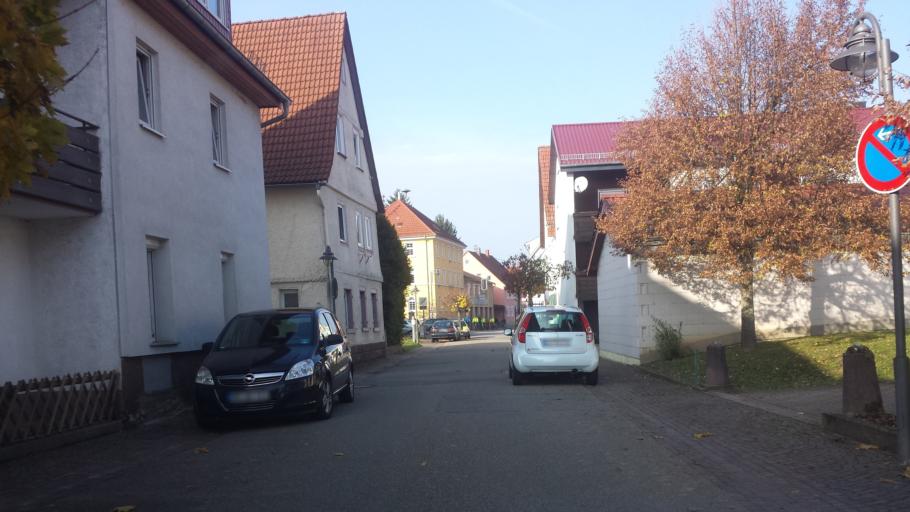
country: DE
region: Baden-Wuerttemberg
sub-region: Karlsruhe Region
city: Eschelbronn
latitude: 49.3195
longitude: 8.8685
